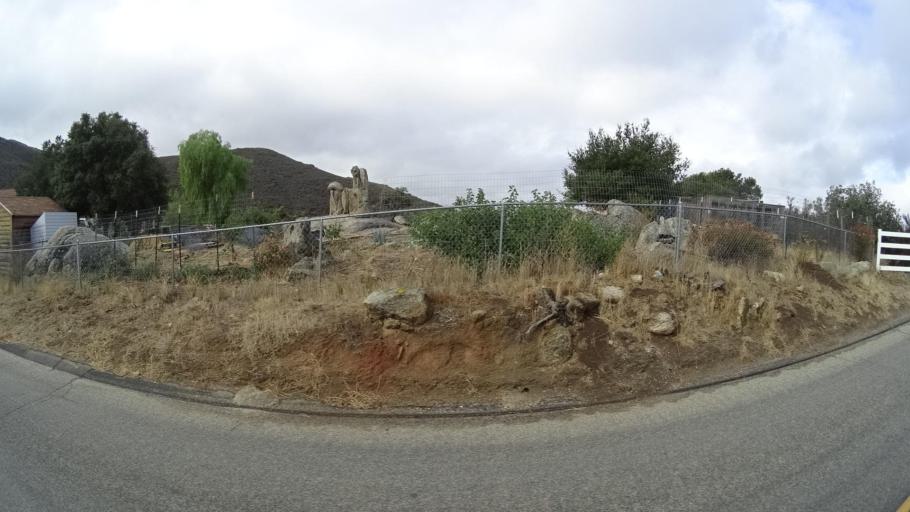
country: MX
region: Baja California
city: Tecate
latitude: 32.6313
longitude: -116.6345
